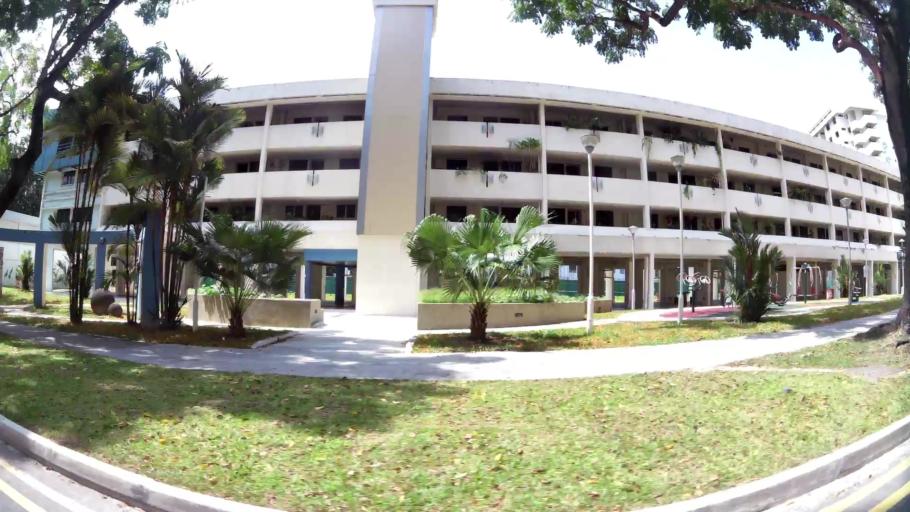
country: SG
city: Singapore
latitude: 1.3699
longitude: 103.8368
